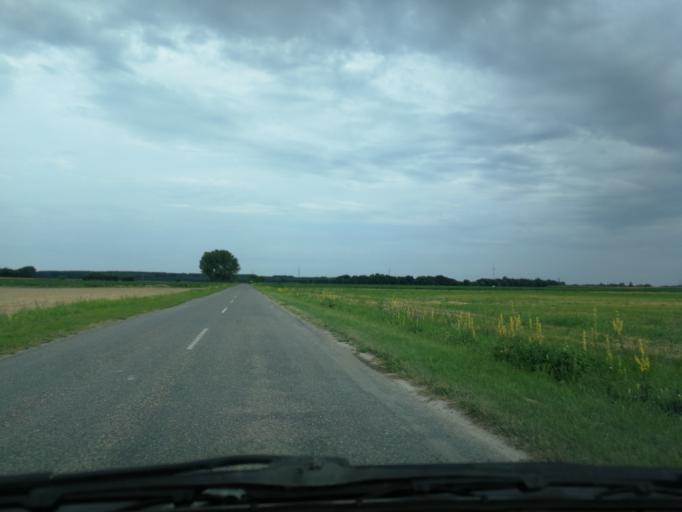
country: HU
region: Bacs-Kiskun
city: Batya
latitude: 46.4525
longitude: 18.9619
